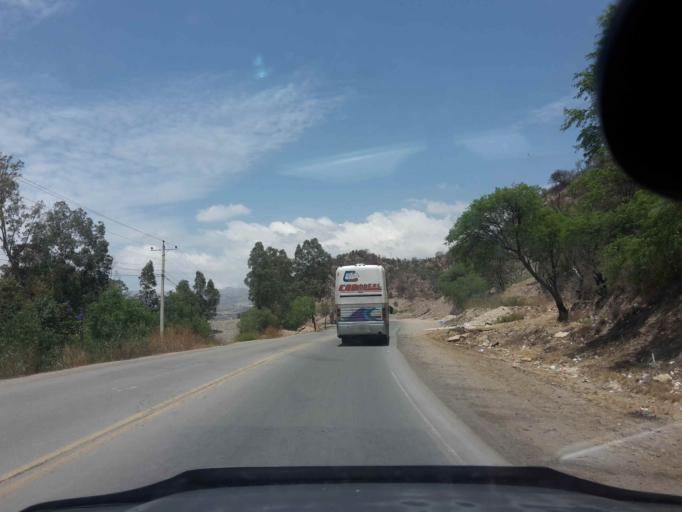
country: BO
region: Cochabamba
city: Sipe Sipe
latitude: -17.5395
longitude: -66.3355
